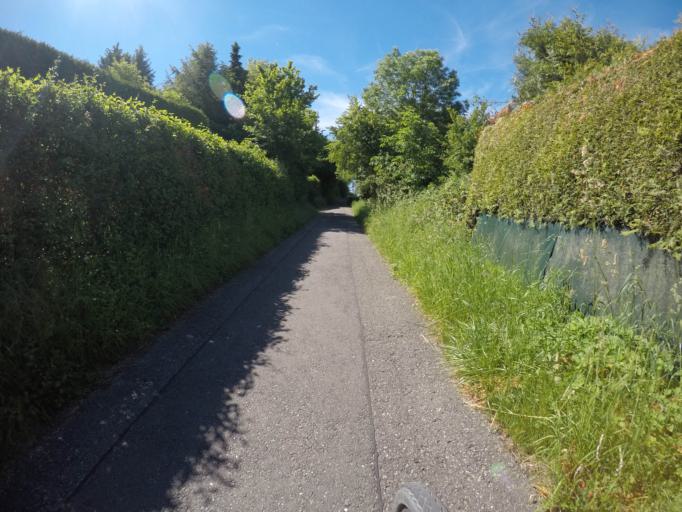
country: DE
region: Baden-Wuerttemberg
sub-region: Karlsruhe Region
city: Ispringen
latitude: 48.9097
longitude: 8.6849
